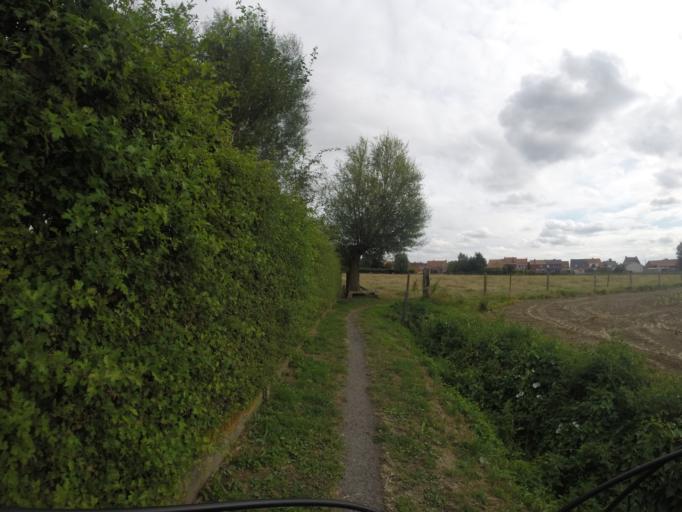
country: BE
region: Flanders
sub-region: Provincie West-Vlaanderen
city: Hooglede
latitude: 50.9447
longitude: 3.0733
